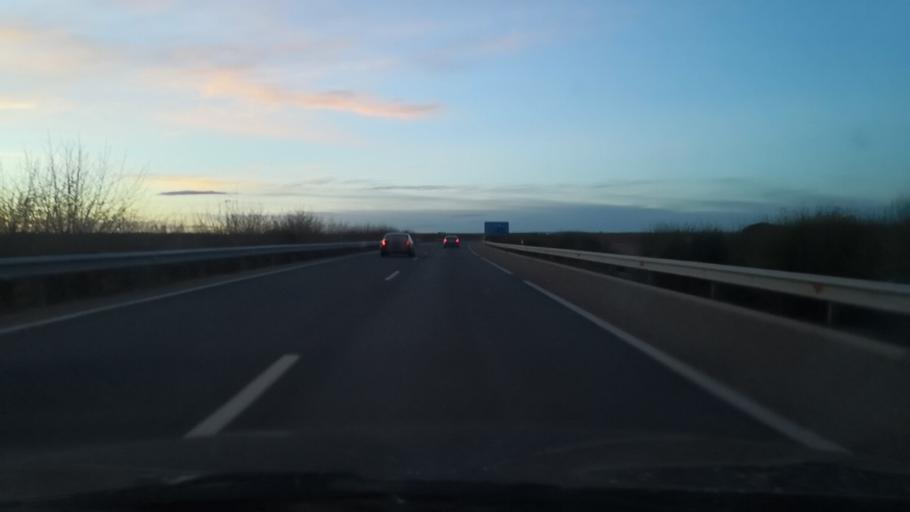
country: ES
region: Castille and Leon
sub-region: Provincia de Zamora
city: Morales de Toro
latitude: 41.5294
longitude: -5.2752
